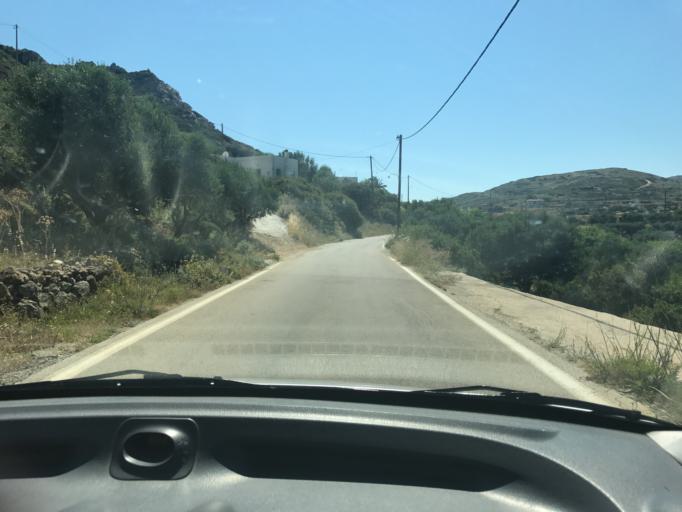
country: GR
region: South Aegean
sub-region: Nomos Dodekanisou
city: Karpathos
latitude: 35.4896
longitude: 27.1596
